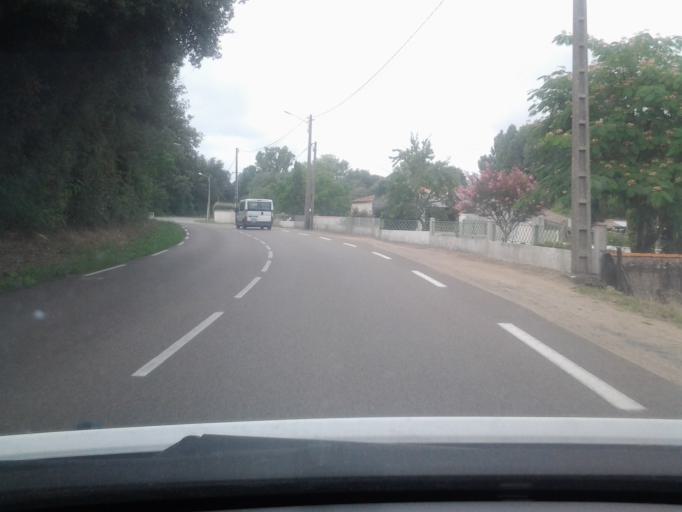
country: FR
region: Pays de la Loire
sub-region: Departement de la Vendee
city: Longeville-sur-Mer
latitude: 46.3973
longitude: -1.4833
